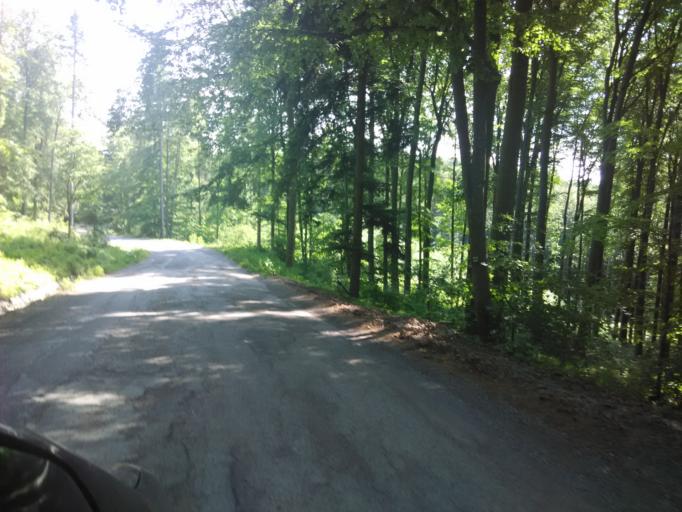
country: SK
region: Banskobystricky
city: Revuca
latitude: 48.6512
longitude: 20.2964
